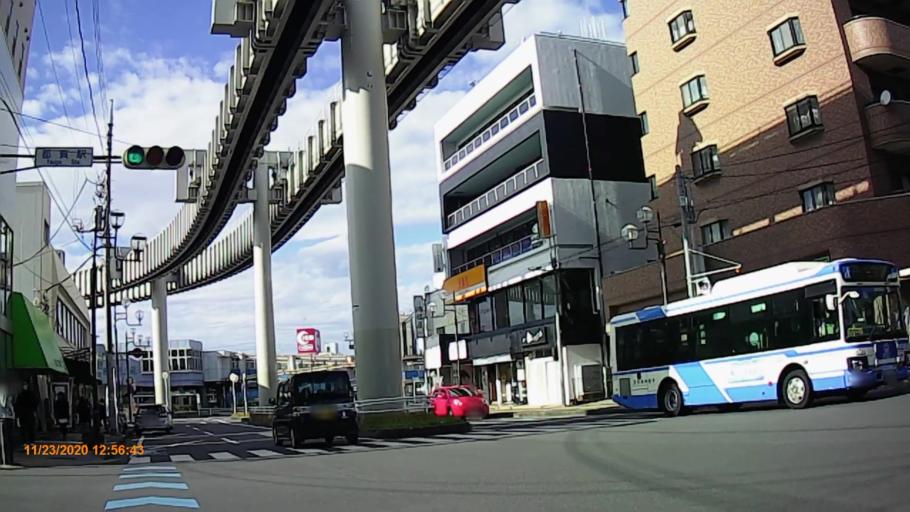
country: JP
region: Chiba
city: Yotsukaido
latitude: 35.6355
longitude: 140.1512
